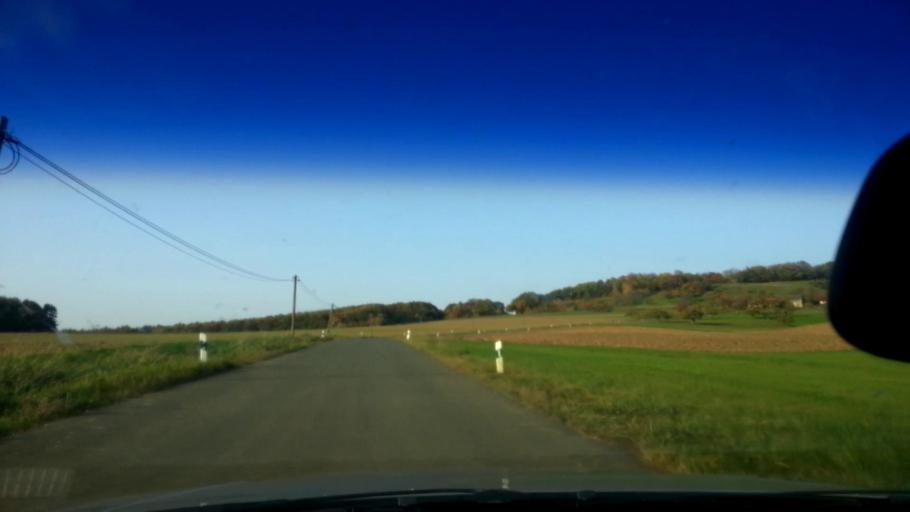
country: DE
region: Bavaria
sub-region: Upper Franconia
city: Schesslitz
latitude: 50.0131
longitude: 11.0199
